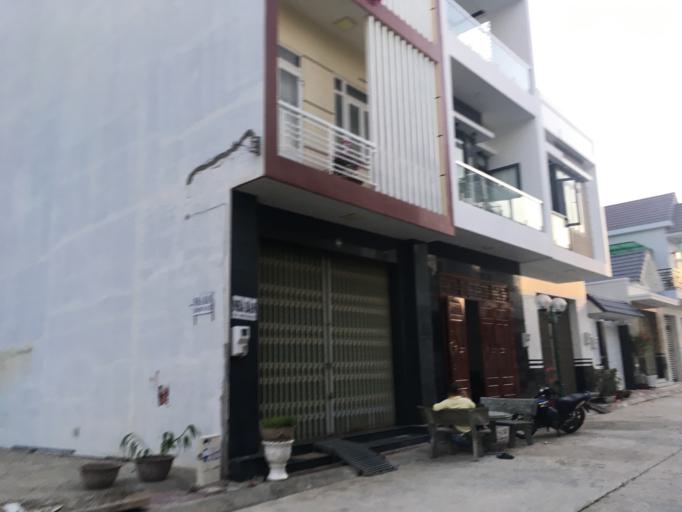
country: VN
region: Ninh Thuan
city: Phan Rang-Thap Cham
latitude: 11.5696
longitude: 108.9973
